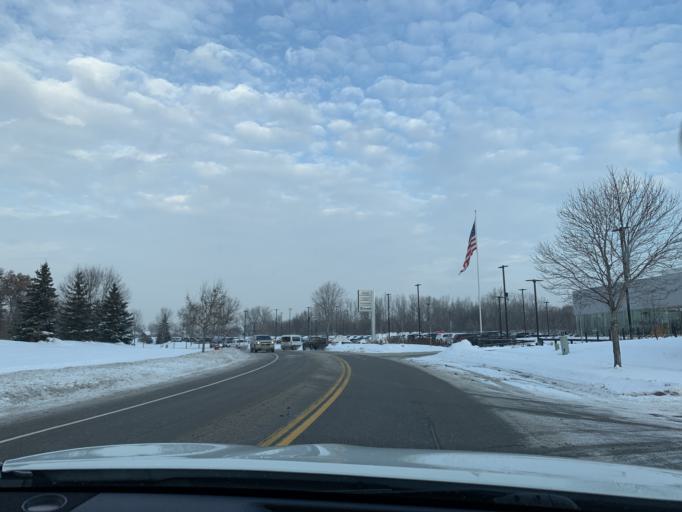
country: US
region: Minnesota
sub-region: Anoka County
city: Coon Rapids
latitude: 45.1603
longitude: -93.2854
